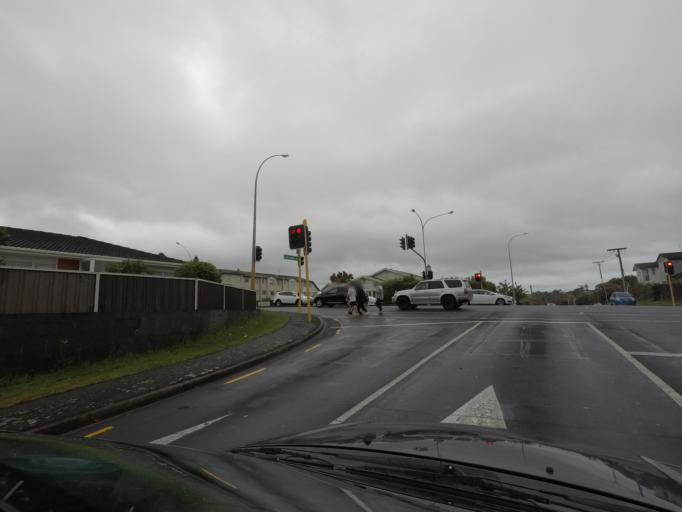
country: NZ
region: Auckland
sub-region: Auckland
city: Auckland
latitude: -36.8843
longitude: 174.7355
